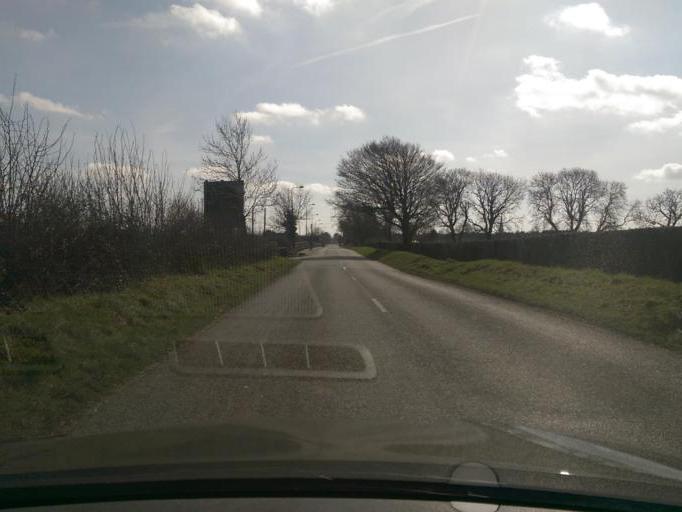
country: IE
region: Leinster
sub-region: Kildare
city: Maynooth
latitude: 53.3937
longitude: -6.6002
